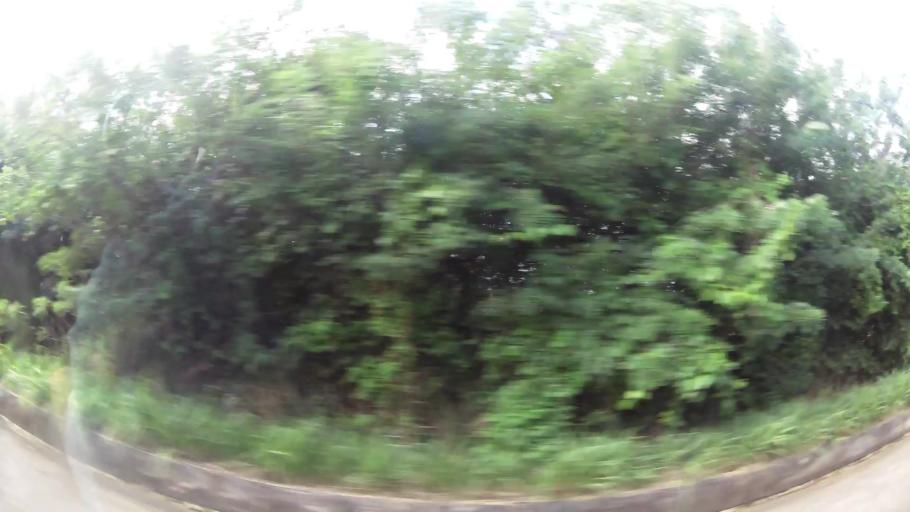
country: MQ
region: Martinique
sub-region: Martinique
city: Le Vauclin
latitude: 14.5737
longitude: -60.8632
